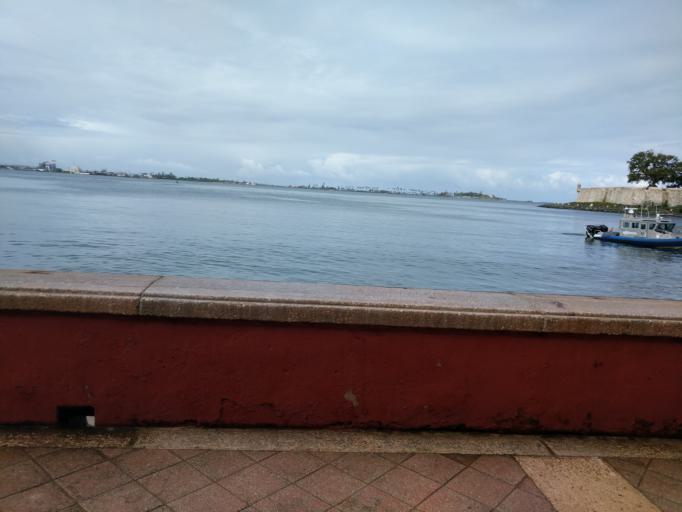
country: PR
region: San Juan
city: San Juan
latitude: 18.4644
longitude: -66.1196
